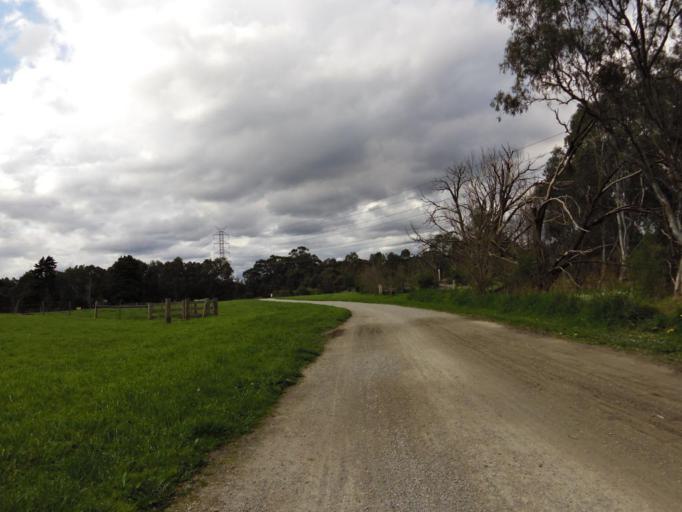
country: AU
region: Victoria
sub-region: Manningham
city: Bulleen
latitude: -37.7710
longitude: 145.0707
